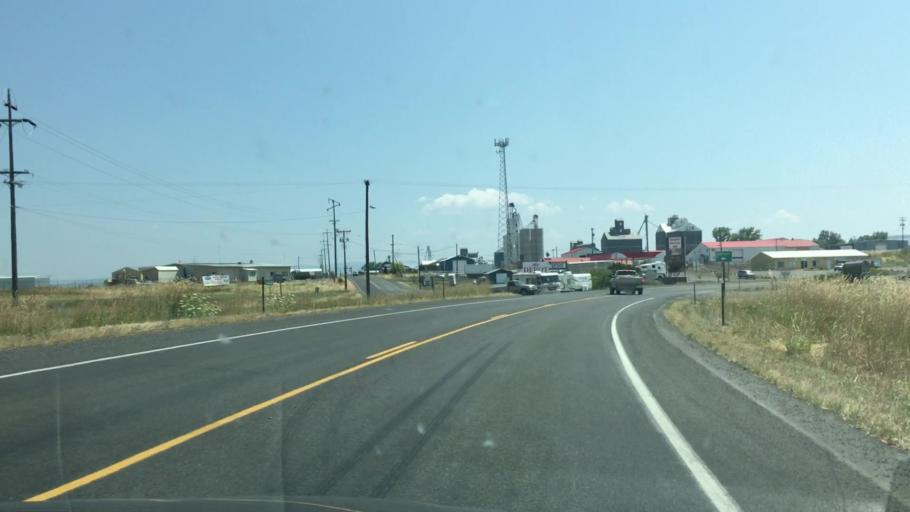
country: US
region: Idaho
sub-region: Idaho County
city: Grangeville
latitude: 45.9359
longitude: -116.1356
